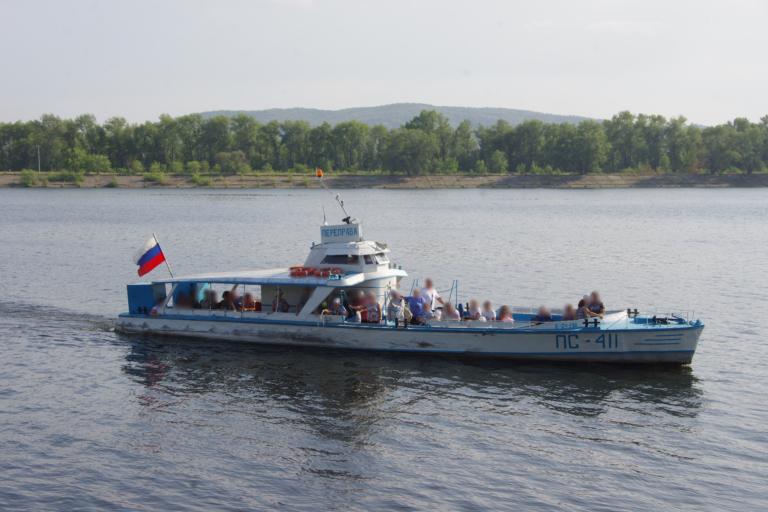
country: RU
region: Samara
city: Zhigulevsk
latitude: 53.4624
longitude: 49.5350
